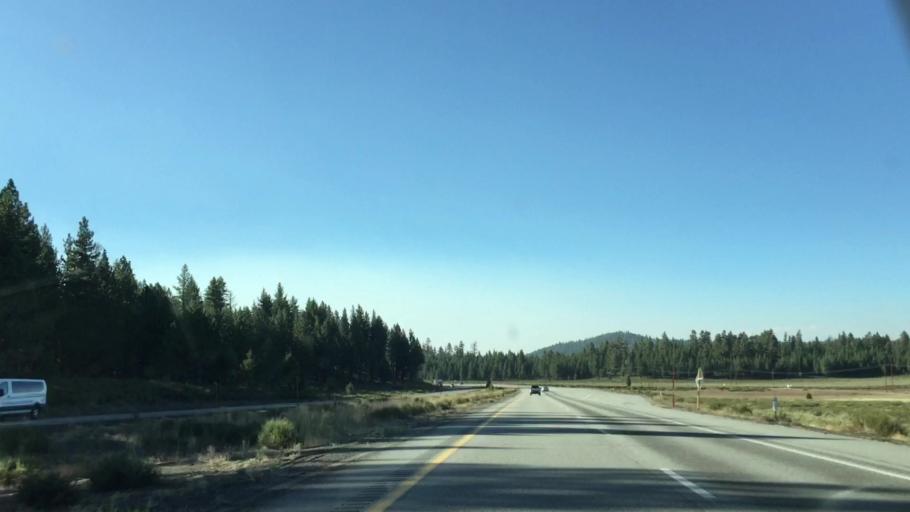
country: US
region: California
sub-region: Mono County
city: Mammoth Lakes
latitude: 37.6866
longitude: -118.9418
